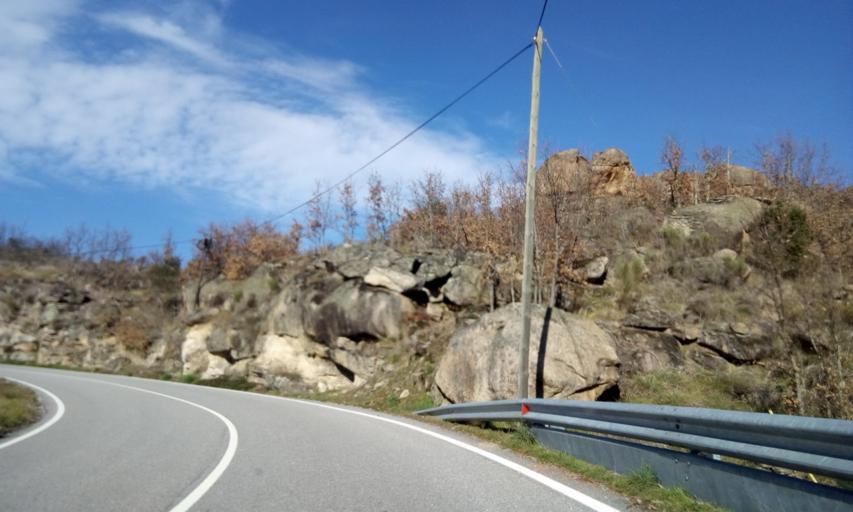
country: ES
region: Castille and Leon
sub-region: Provincia de Salamanca
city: Fuentes de Onoro
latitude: 40.6173
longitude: -6.9134
